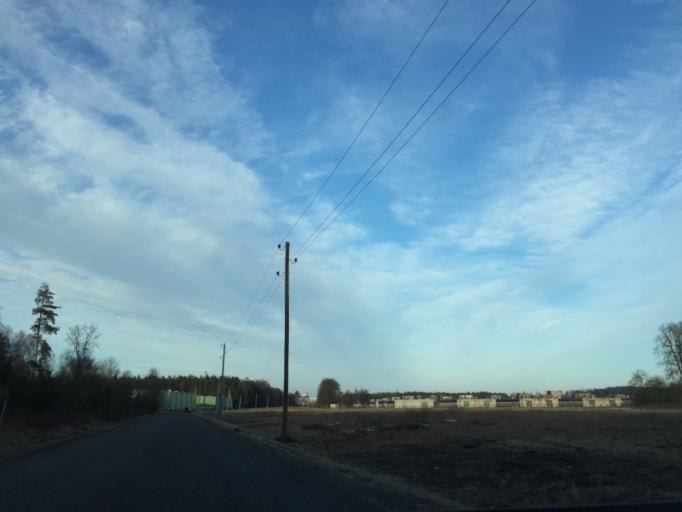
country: LV
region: Kekava
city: Kekava
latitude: 56.8226
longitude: 24.1890
